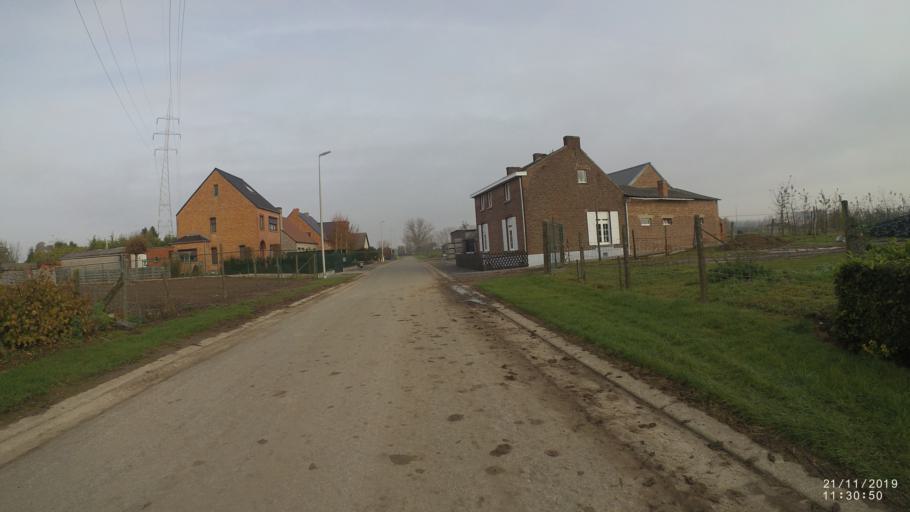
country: BE
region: Flanders
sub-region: Provincie Limburg
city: Sint-Truiden
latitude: 50.8246
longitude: 5.2273
